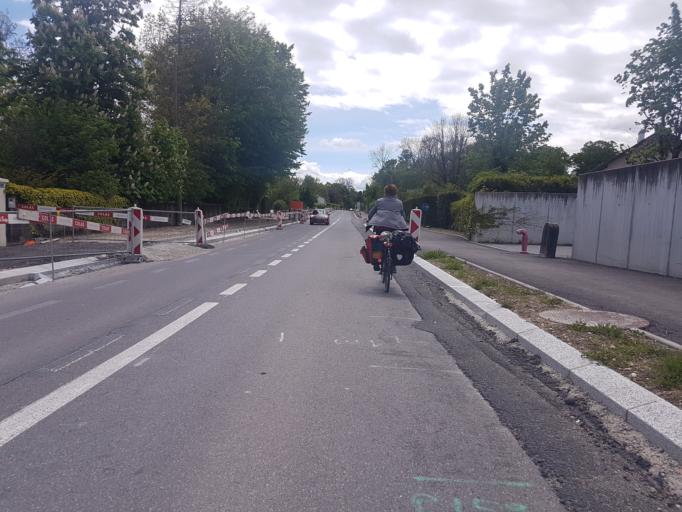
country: CH
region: Vaud
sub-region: Nyon District
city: Founex
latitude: 46.3260
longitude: 6.1987
